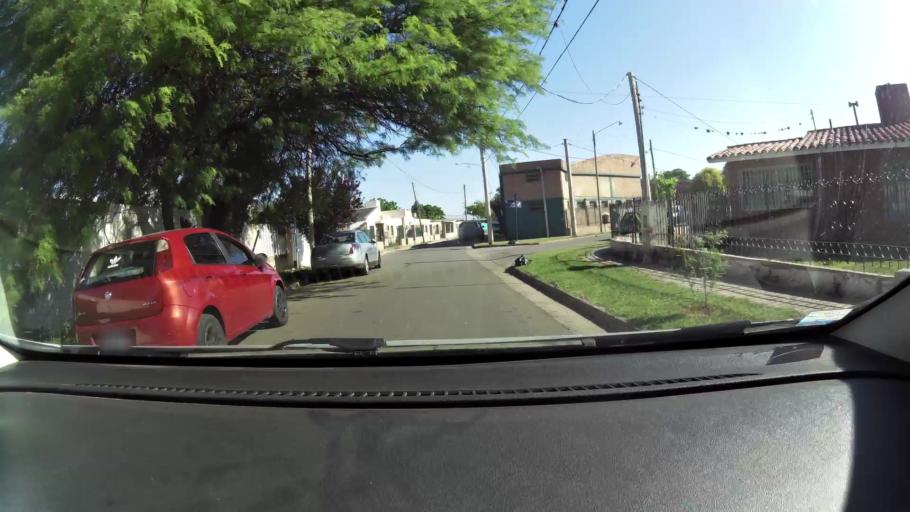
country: AR
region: Cordoba
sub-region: Departamento de Capital
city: Cordoba
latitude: -31.3640
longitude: -64.1913
